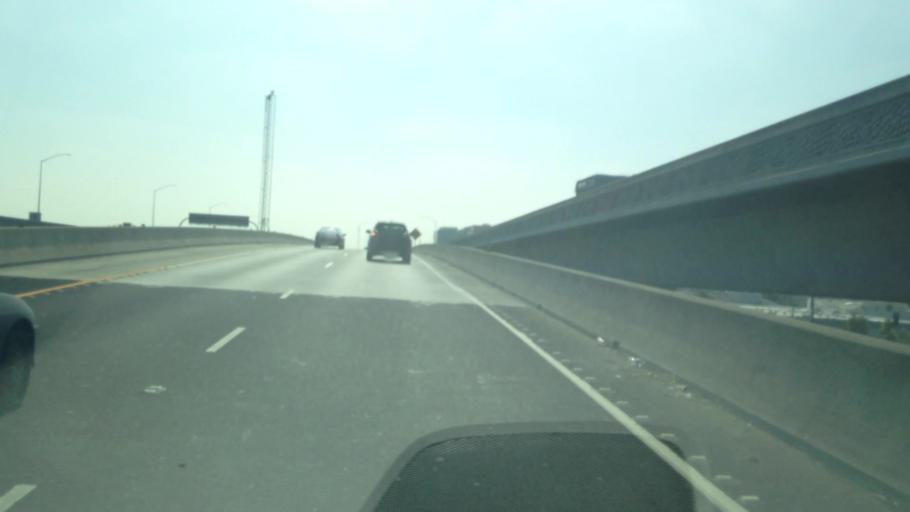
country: US
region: California
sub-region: Los Angeles County
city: El Segundo
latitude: 33.9313
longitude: -118.3969
